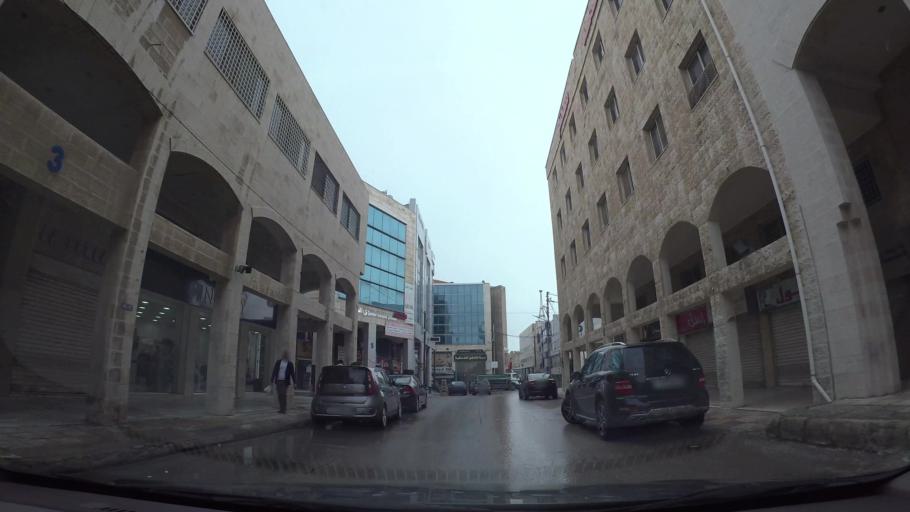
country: JO
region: Amman
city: Wadi as Sir
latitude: 31.9577
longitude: 35.8682
